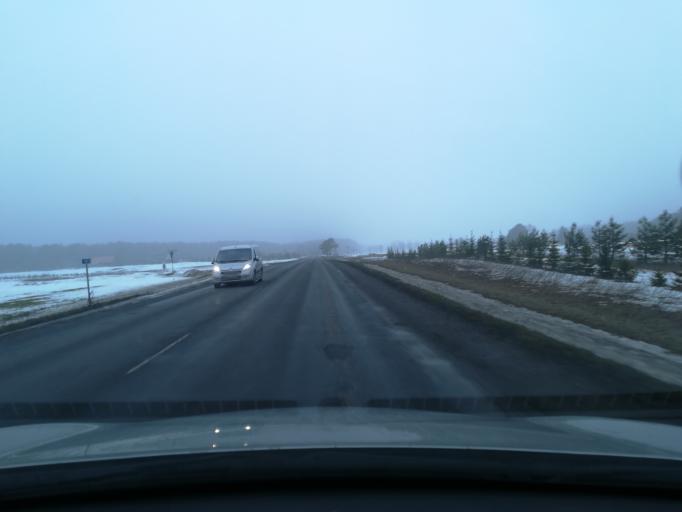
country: EE
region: Harju
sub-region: Raasiku vald
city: Arukula
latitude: 59.3517
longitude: 25.0841
